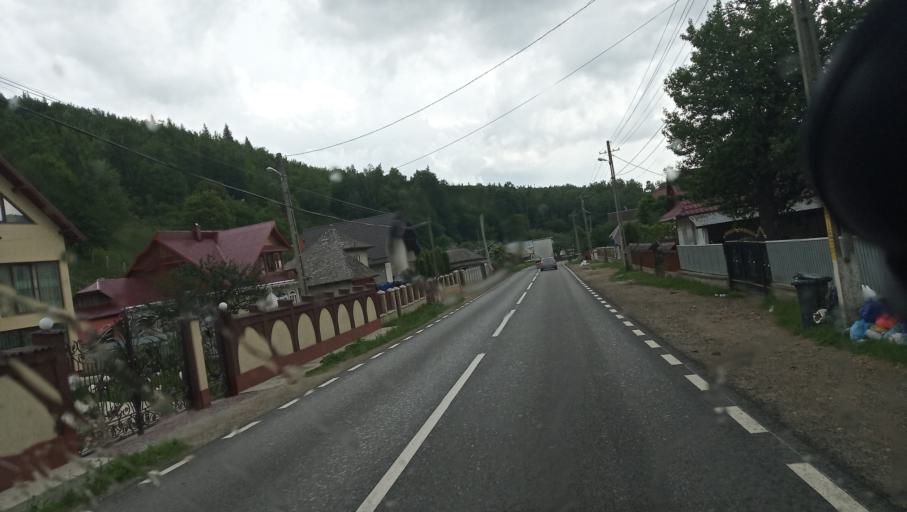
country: RO
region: Neamt
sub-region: Comuna Pipirig
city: Stanca
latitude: 47.2286
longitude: 26.1050
